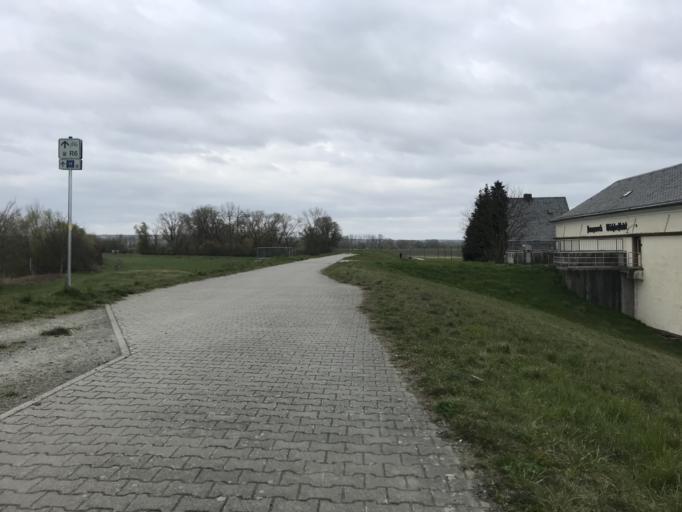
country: DE
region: Rheinland-Pfalz
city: Oppenheim
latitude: 49.8627
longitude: 8.3773
